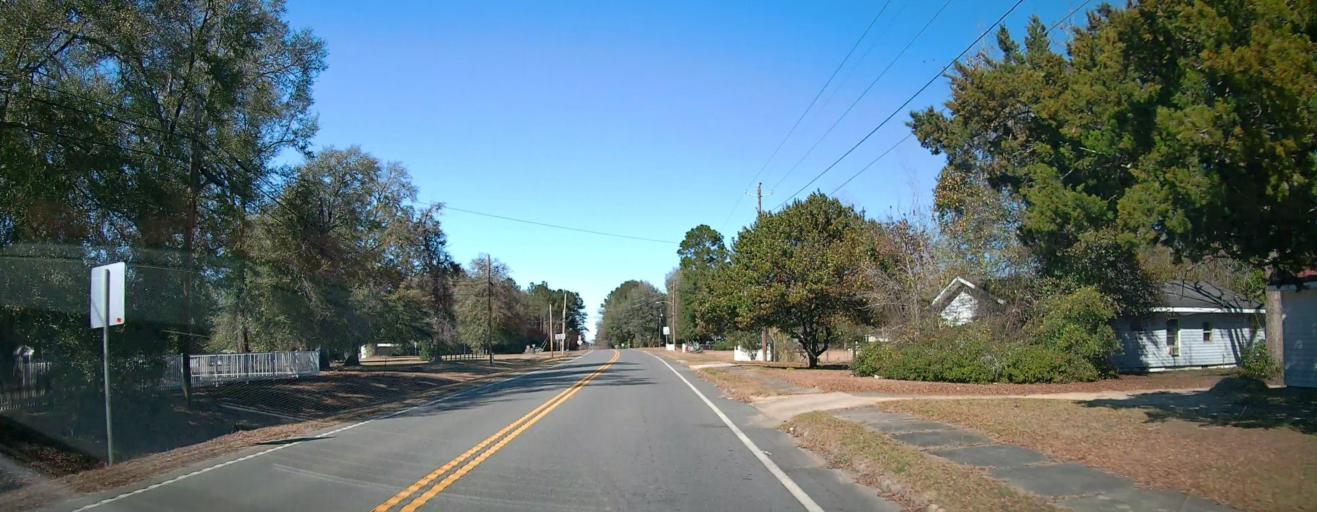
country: US
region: Georgia
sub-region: Macon County
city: Oglethorpe
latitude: 32.3041
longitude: -84.0656
